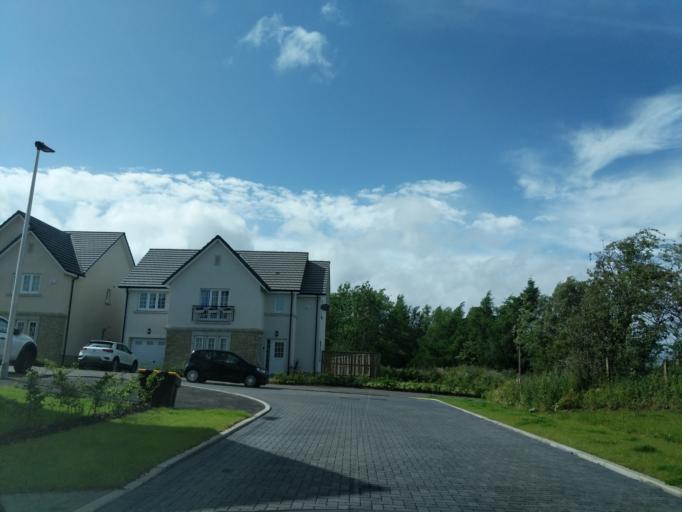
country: GB
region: Scotland
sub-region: Midlothian
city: Loanhead
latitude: 55.8587
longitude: -3.1748
